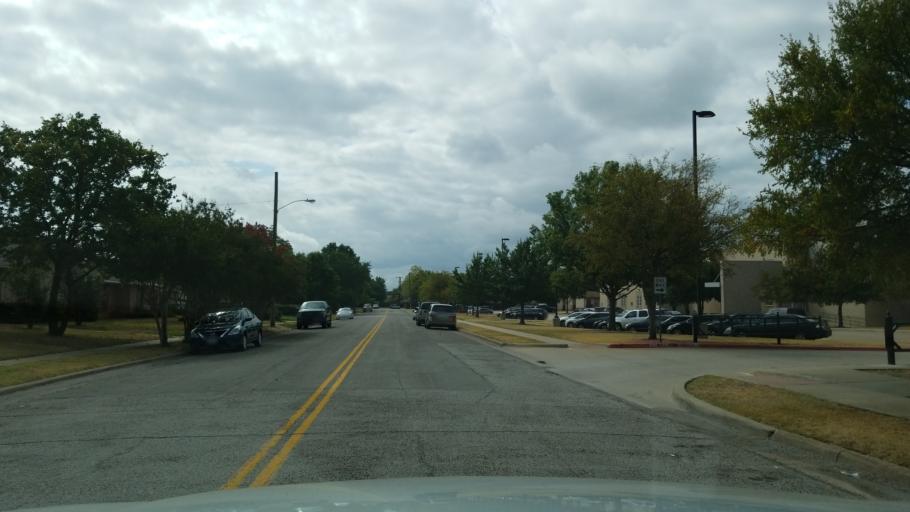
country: US
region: Texas
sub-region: Dallas County
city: Garland
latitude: 32.8716
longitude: -96.6869
